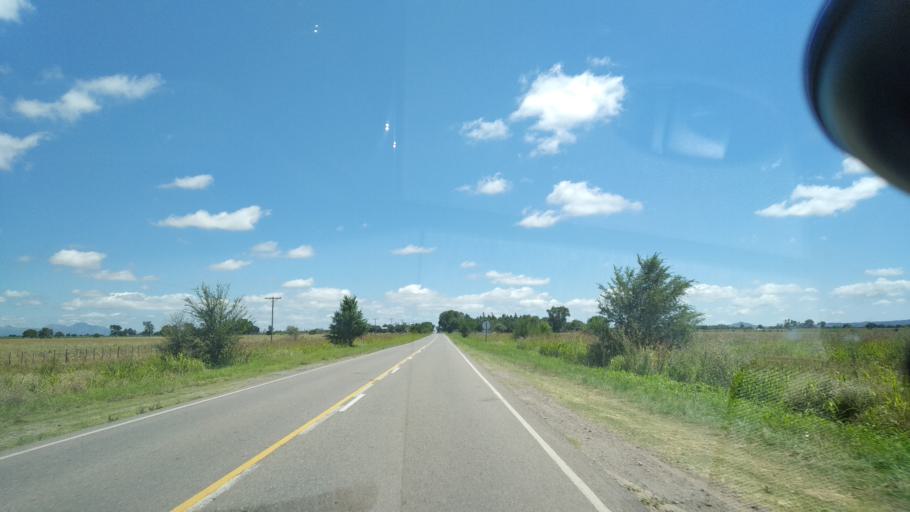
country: AR
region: Cordoba
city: Villa Cura Brochero
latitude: -31.5425
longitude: -65.1118
